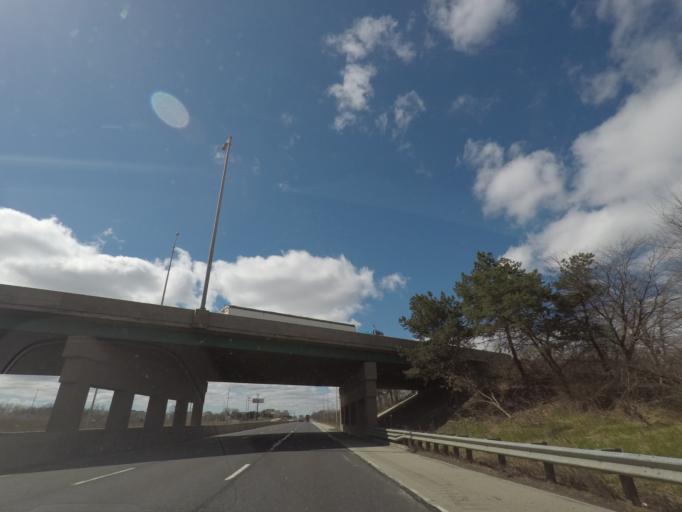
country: US
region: Illinois
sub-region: Will County
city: Shorewood
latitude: 41.5223
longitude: -88.1885
